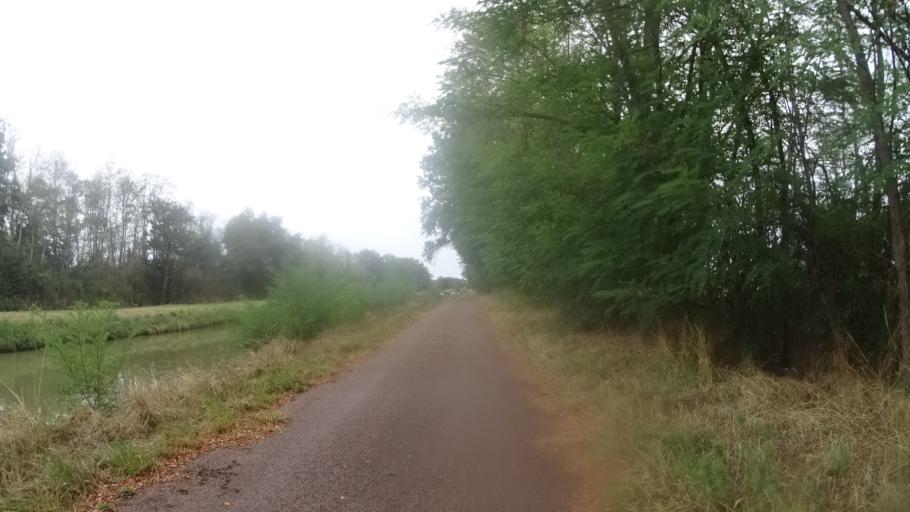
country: FR
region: Bourgogne
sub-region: Departement de la Nievre
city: Imphy
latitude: 46.8914
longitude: 3.2458
